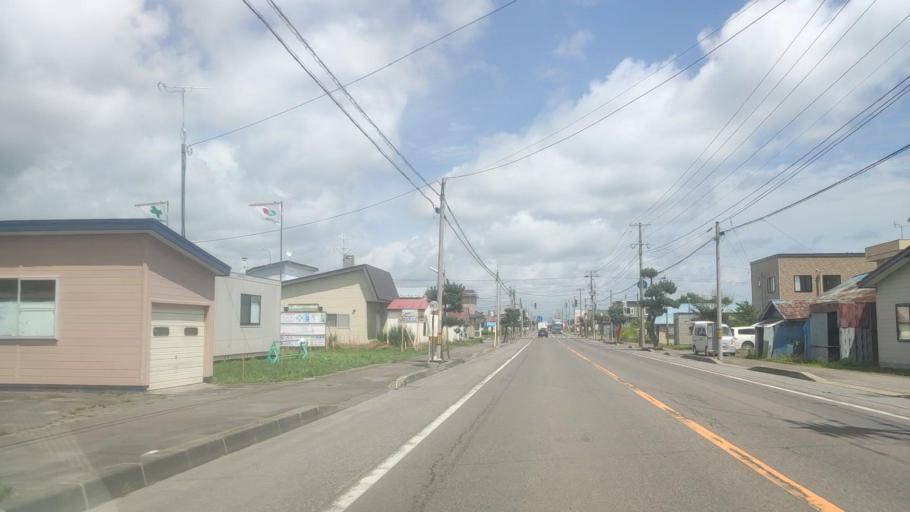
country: JP
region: Hokkaido
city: Niseko Town
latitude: 42.4351
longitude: 140.3209
